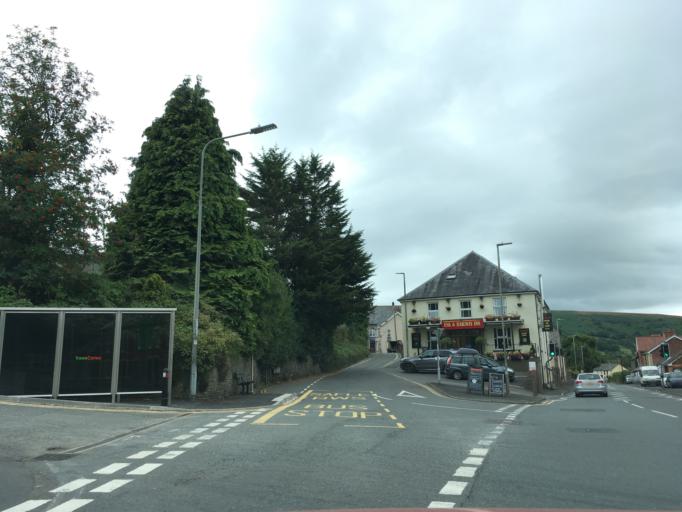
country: GB
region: Wales
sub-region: Sir Powys
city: Cray
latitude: 51.9476
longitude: -3.5679
